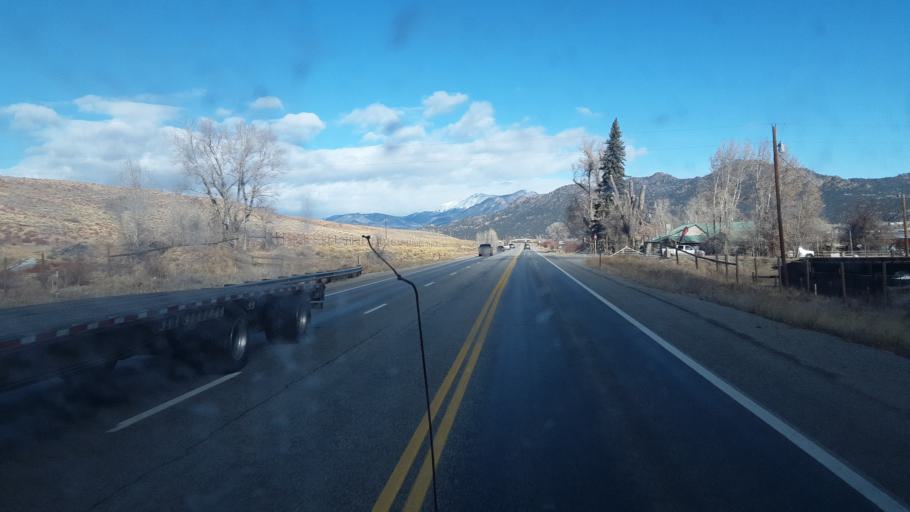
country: US
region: Colorado
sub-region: Chaffee County
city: Buena Vista
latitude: 38.7951
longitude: -106.1143
